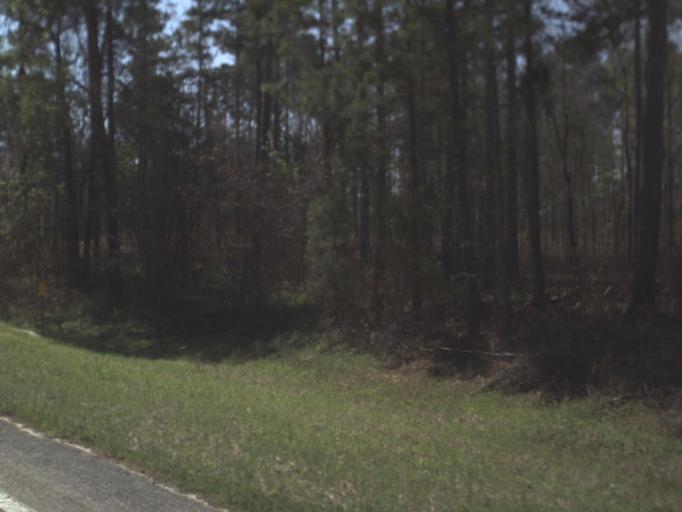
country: US
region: Florida
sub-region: Jefferson County
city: Monticello
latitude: 30.3891
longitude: -84.0111
